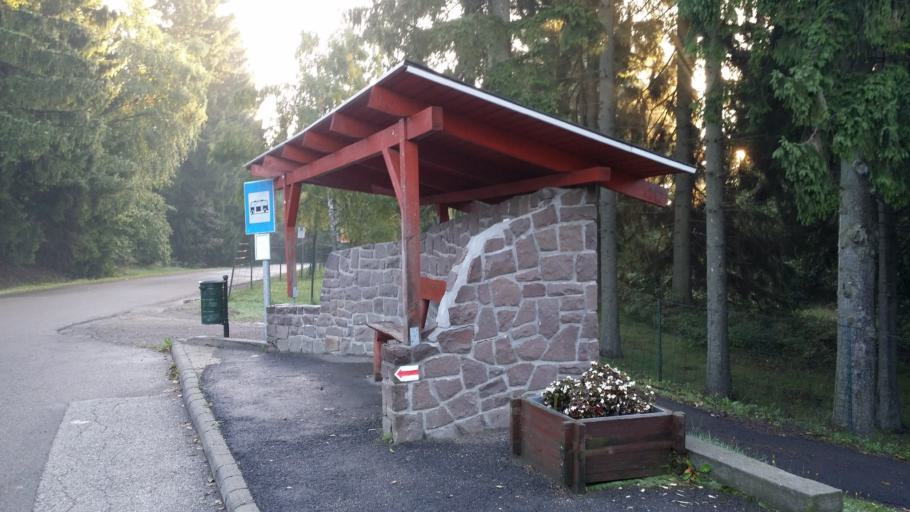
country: HU
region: Heves
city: Paradsasvar
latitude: 47.9143
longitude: 19.9203
